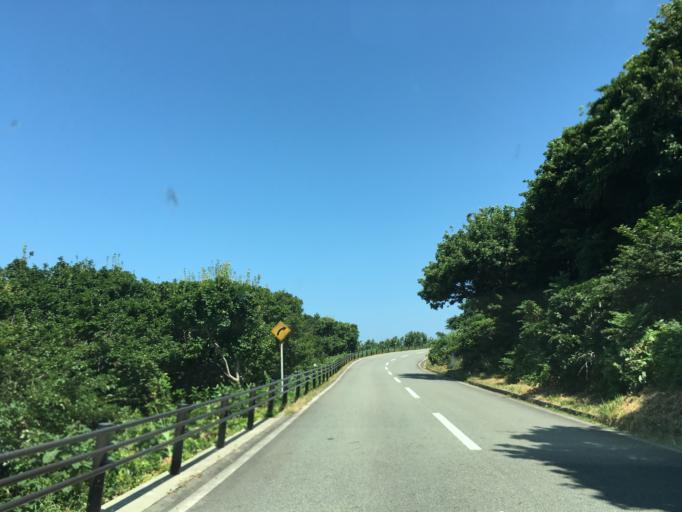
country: JP
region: Akita
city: Tenno
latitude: 39.8727
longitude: 139.7434
